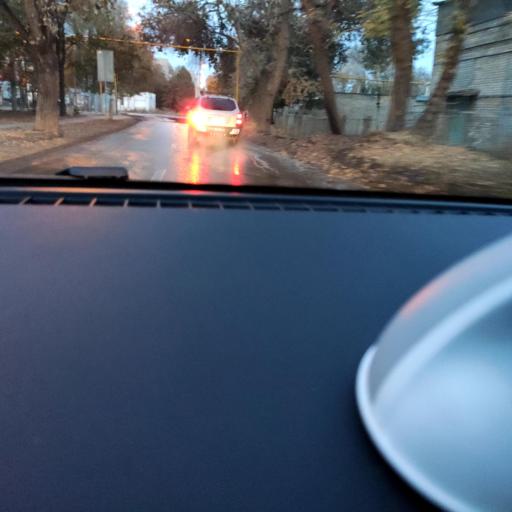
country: RU
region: Samara
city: Samara
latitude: 53.1984
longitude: 50.2484
